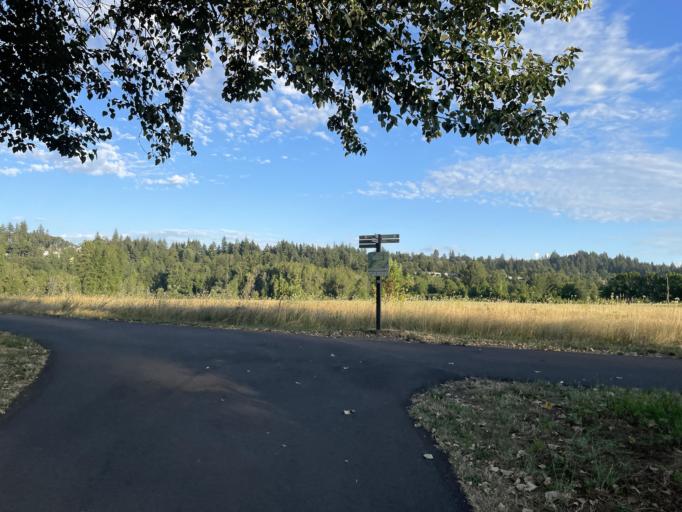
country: US
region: Oregon
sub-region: Marion County
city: Salem
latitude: 44.9266
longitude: -123.0623
